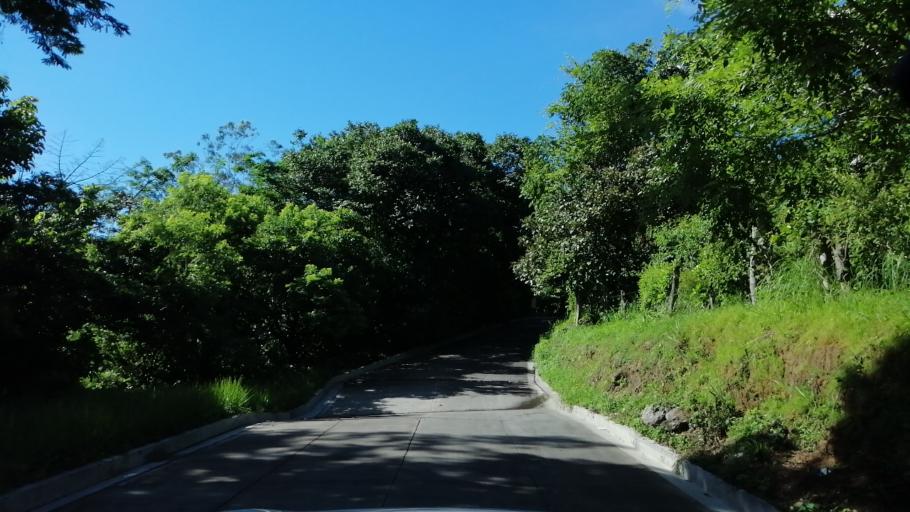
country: SV
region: Morazan
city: Corinto
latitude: 13.8076
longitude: -87.9720
